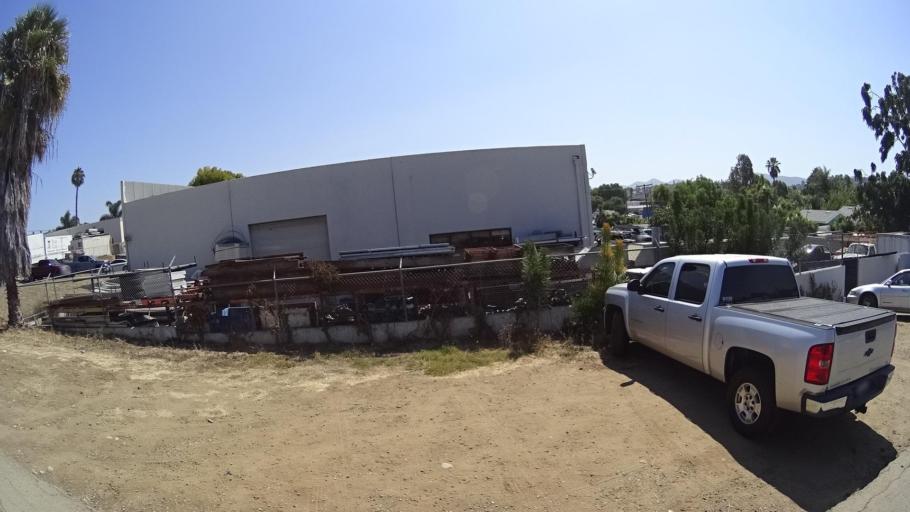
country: US
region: California
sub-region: San Diego County
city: Lake San Marcos
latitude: 33.1633
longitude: -117.2067
